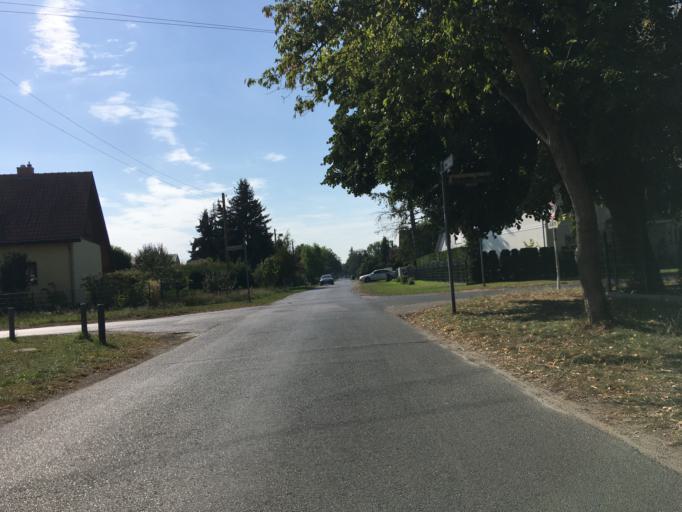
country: DE
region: Berlin
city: Mahlsdorf
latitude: 52.4899
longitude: 13.6026
